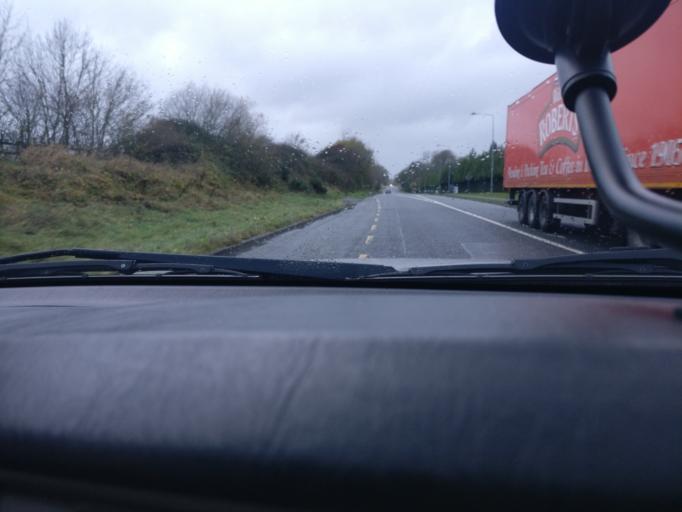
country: IE
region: Leinster
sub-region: Kildare
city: Kilcock
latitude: 53.4067
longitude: -6.6873
